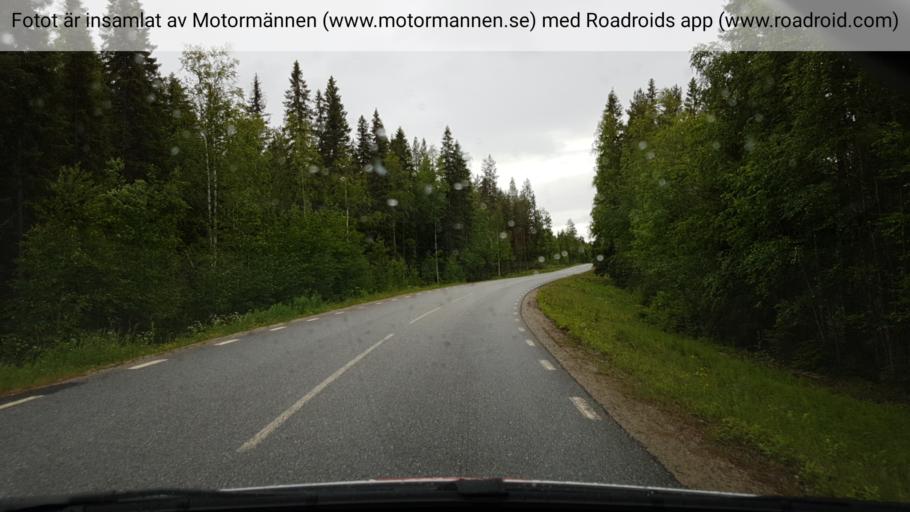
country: SE
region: Vaesterbotten
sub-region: Bjurholms Kommun
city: Bjurholm
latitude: 64.0828
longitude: 19.3472
